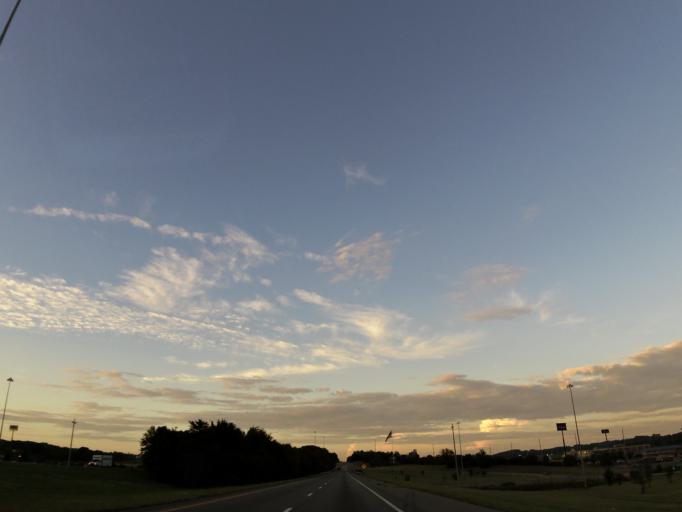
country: US
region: Tennessee
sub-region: McMinn County
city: Athens
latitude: 35.4639
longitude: -84.6504
